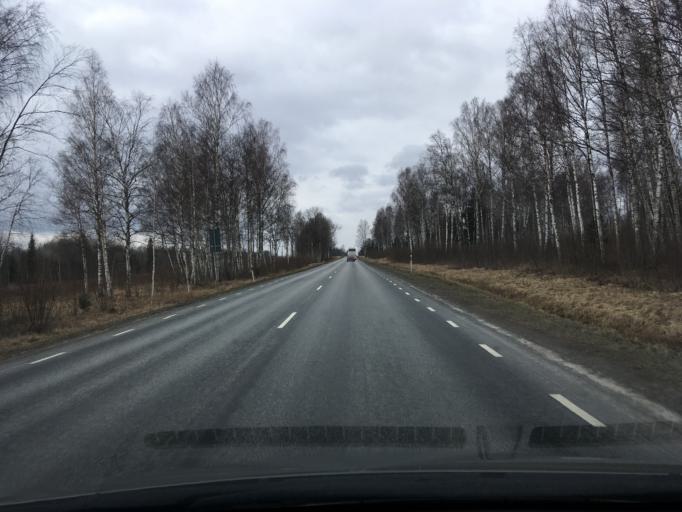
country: EE
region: Laeaene
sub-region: Lihula vald
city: Lihula
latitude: 58.5405
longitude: 24.0098
